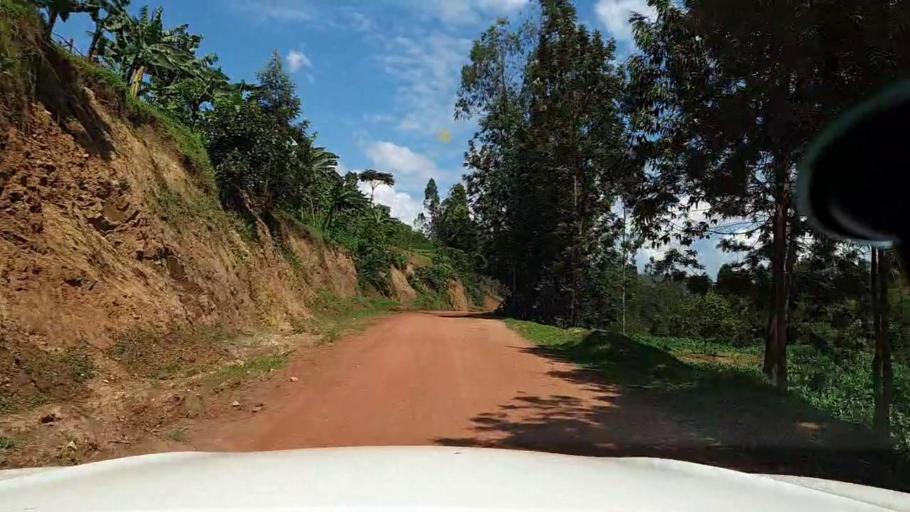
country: RW
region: Kigali
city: Kigali
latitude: -1.7729
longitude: 29.8743
